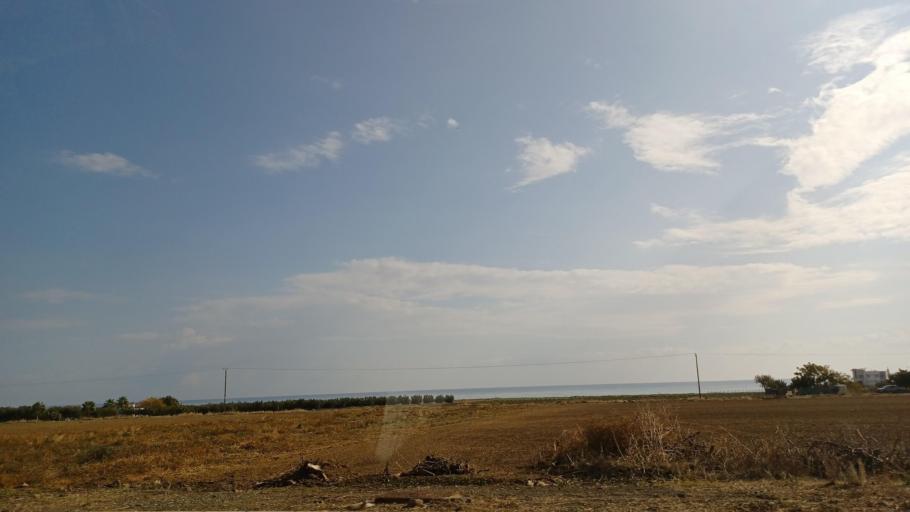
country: CY
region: Larnaka
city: Tersefanou
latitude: 34.8065
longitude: 33.5275
